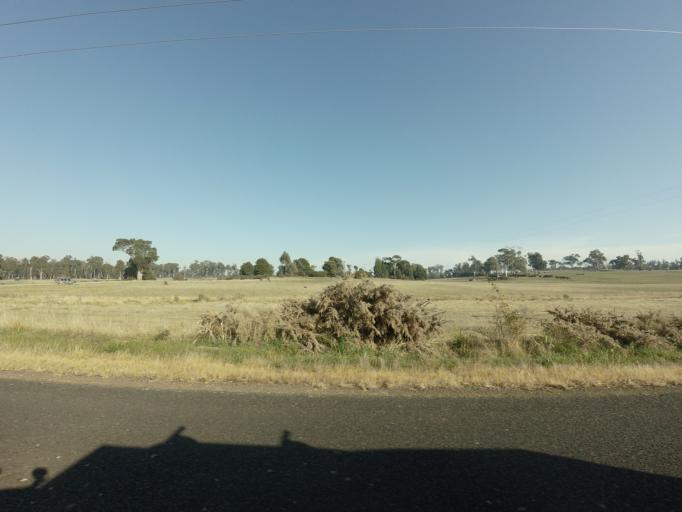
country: AU
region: Tasmania
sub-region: Northern Midlands
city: Longford
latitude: -41.5432
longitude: 146.9917
